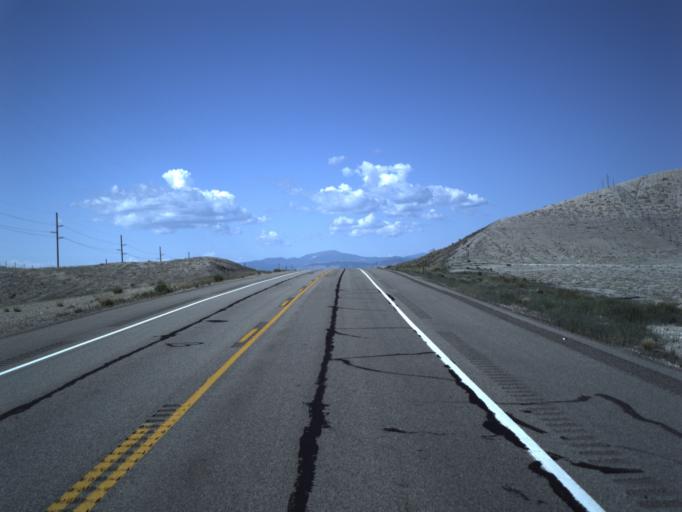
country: US
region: Utah
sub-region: Emery County
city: Ferron
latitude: 38.9525
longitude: -111.2074
